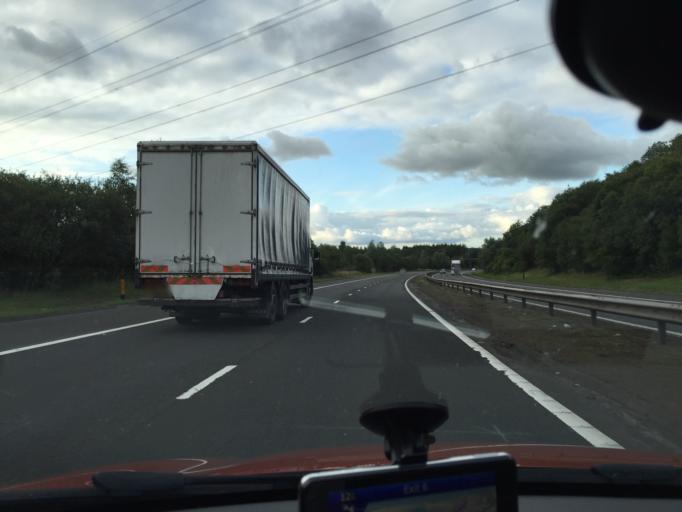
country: GB
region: Scotland
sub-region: North Lanarkshire
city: Chryston
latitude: 55.8798
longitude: -4.0814
